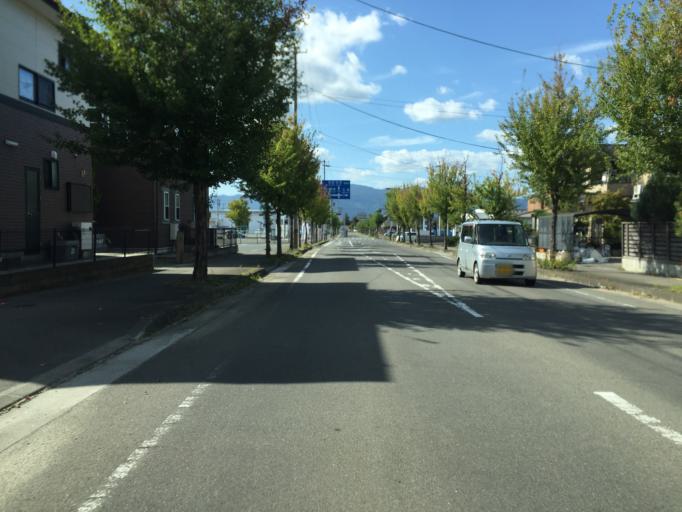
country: JP
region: Fukushima
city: Yanagawamachi-saiwaicho
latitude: 37.8505
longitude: 140.6057
